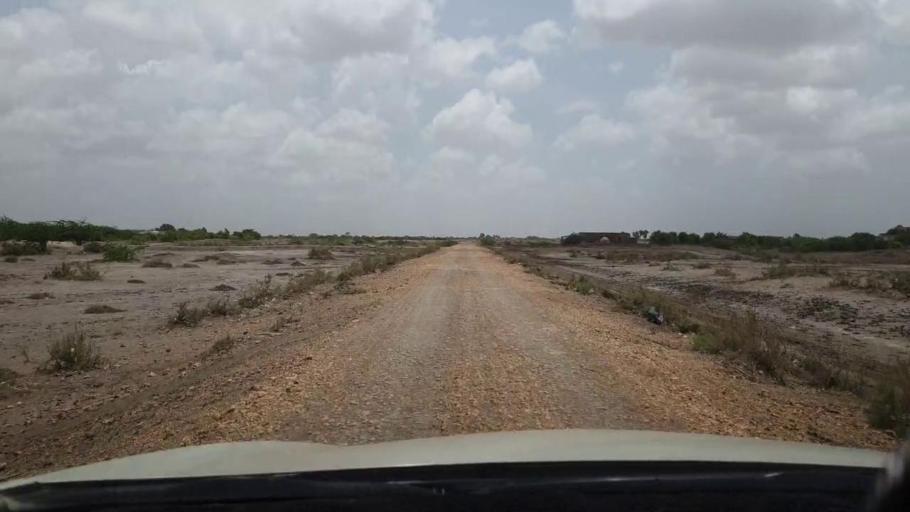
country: PK
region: Sindh
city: Kadhan
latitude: 24.3969
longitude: 68.9362
